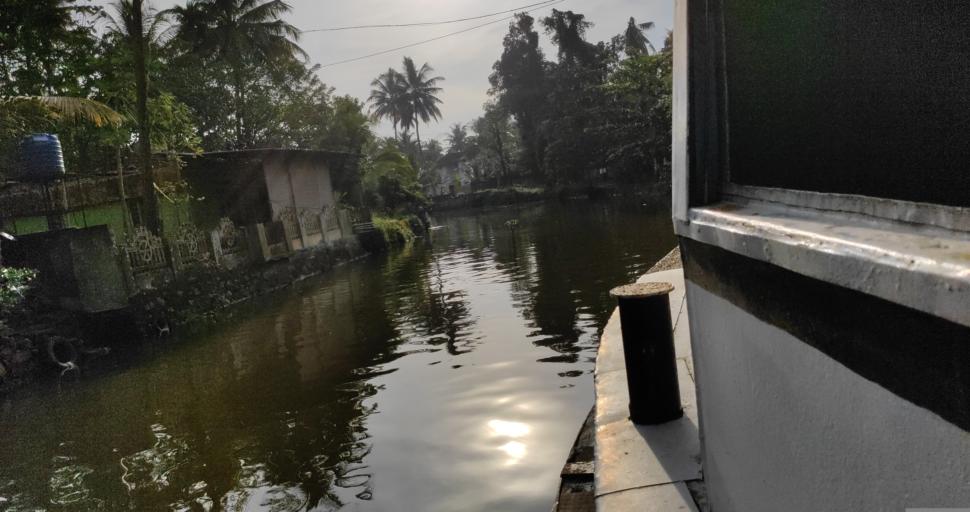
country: IN
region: Kerala
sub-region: Kottayam
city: Kottayam
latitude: 9.5968
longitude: 76.4283
